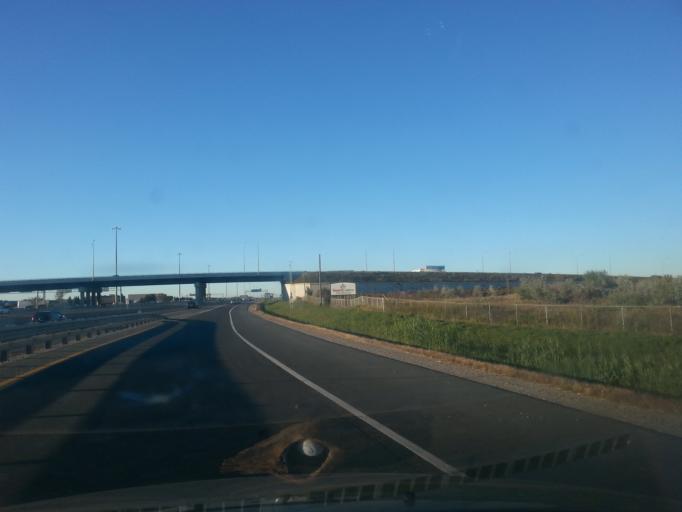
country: CA
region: Ontario
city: Concord
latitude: 43.7935
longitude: -79.5391
